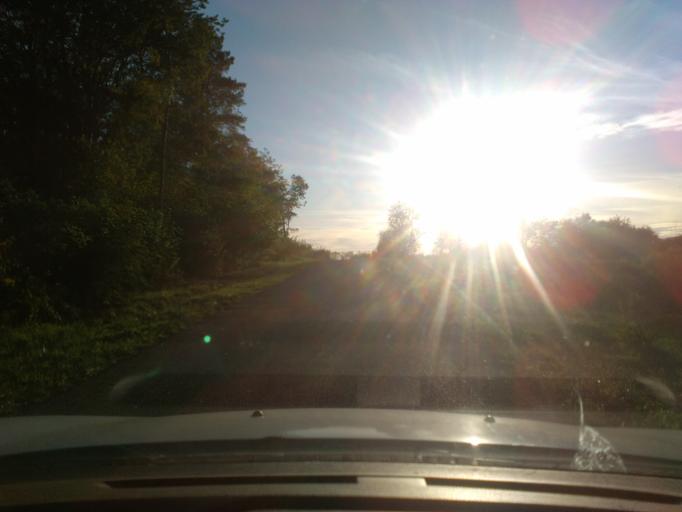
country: FR
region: Lorraine
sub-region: Departement des Vosges
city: Vincey
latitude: 48.3298
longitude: 6.3105
